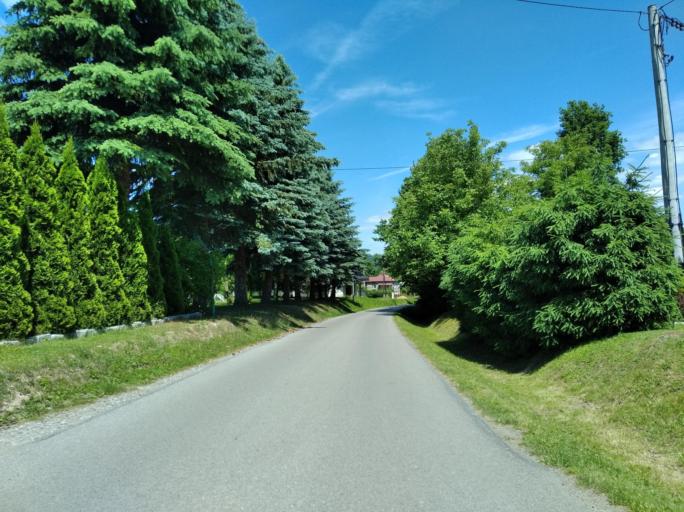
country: PL
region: Subcarpathian Voivodeship
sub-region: Powiat krosnienski
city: Wojaszowka
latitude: 49.7798
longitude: 21.6649
